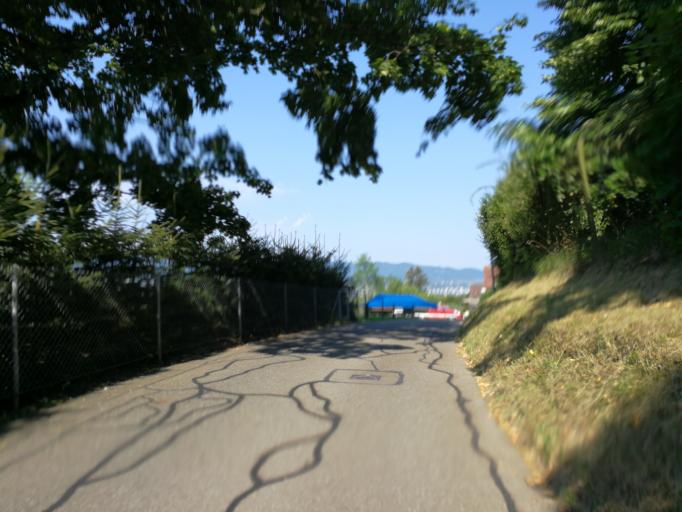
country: CH
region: Zurich
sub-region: Bezirk Meilen
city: Erlenbach / rechts des Dorfbachs oberhalb Bahnlinie
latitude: 47.3054
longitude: 8.6038
